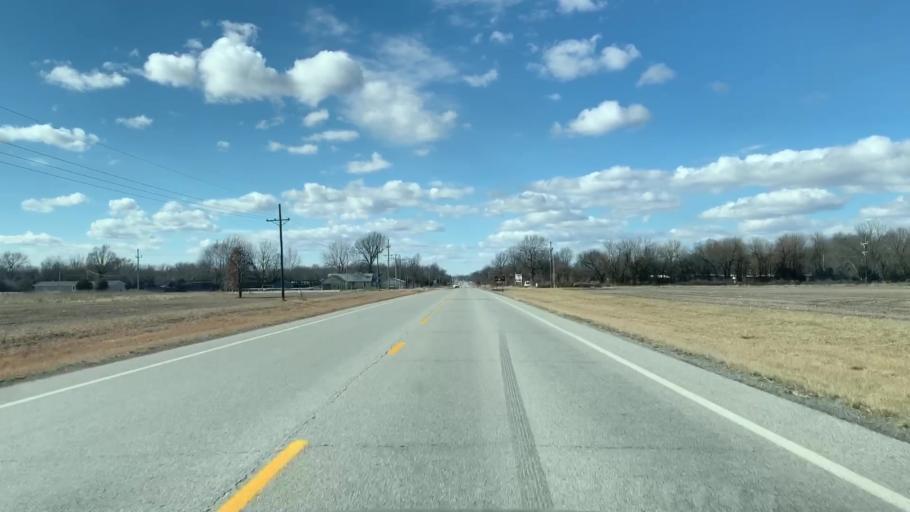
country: US
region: Kansas
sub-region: Cherokee County
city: Columbus
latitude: 37.1781
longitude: -94.8115
